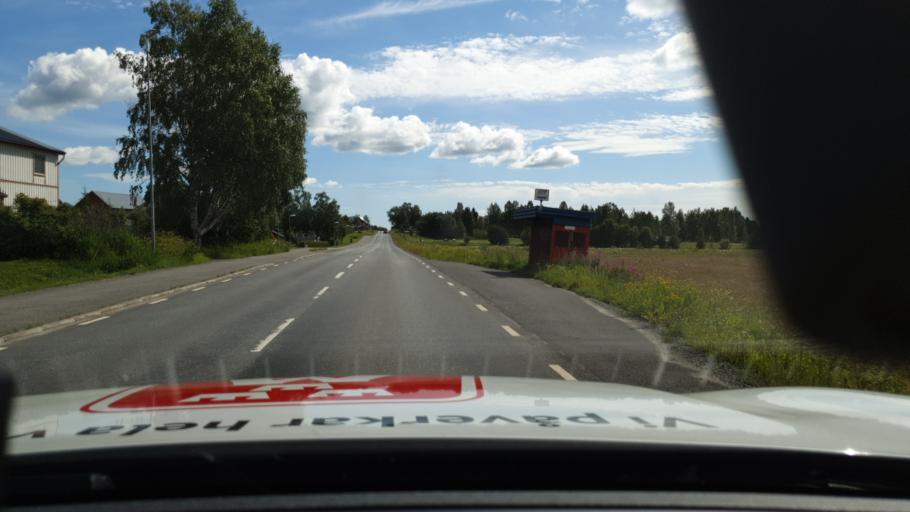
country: SE
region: Norrbotten
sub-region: Lulea Kommun
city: Sodra Sunderbyn
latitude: 65.8091
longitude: 22.0202
